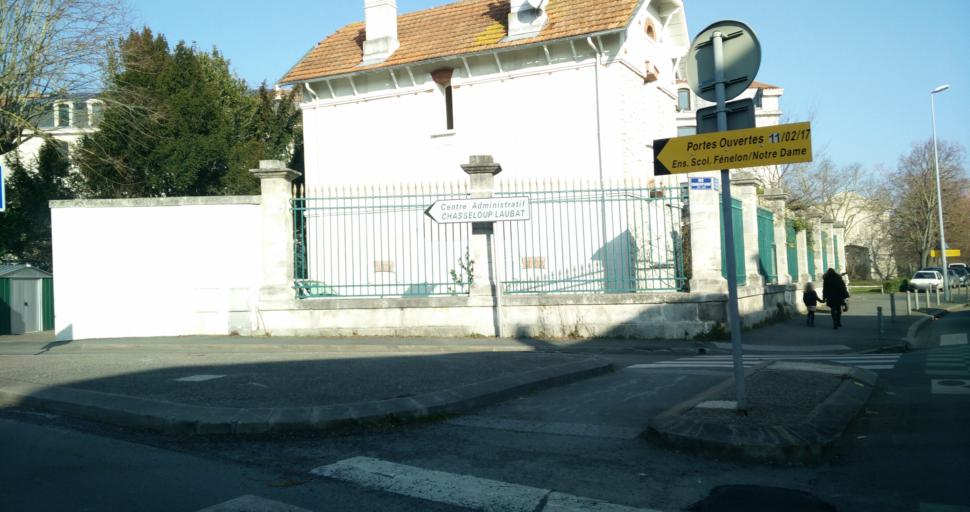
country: FR
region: Poitou-Charentes
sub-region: Departement de la Charente-Maritime
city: La Rochelle
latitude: 46.1663
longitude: -1.1509
